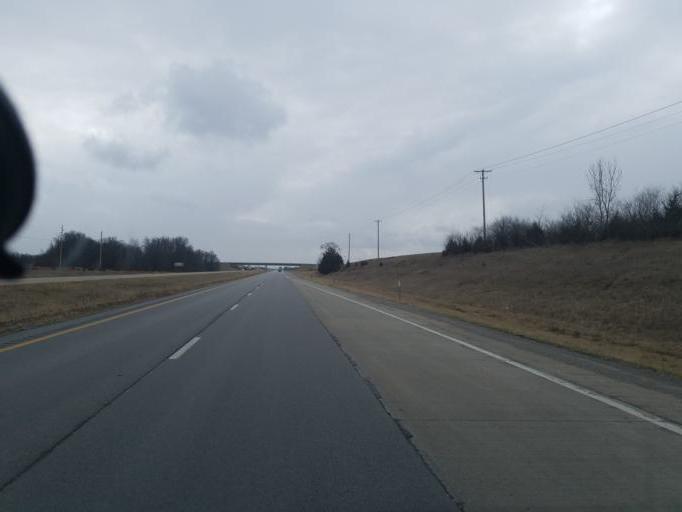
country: US
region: Missouri
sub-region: Randolph County
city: Moberly
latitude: 39.4136
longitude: -92.4124
